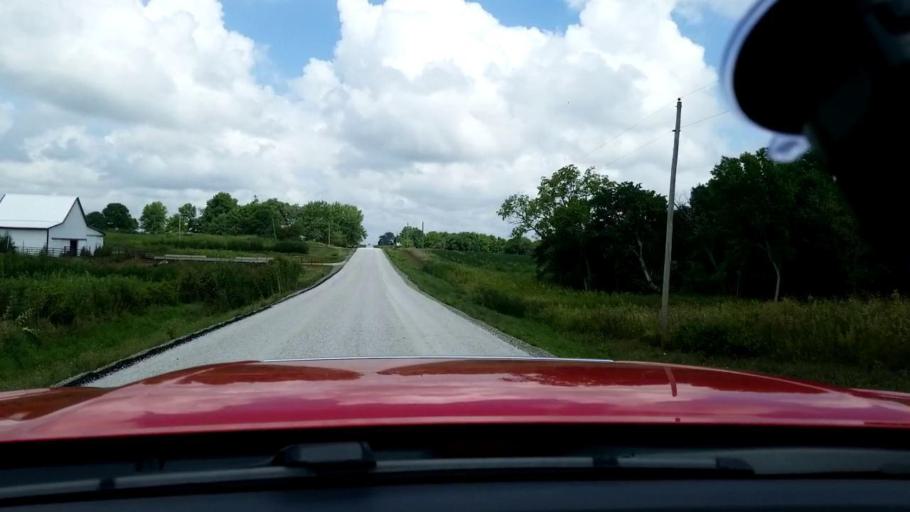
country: US
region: Iowa
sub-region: Decatur County
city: Lamoni
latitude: 40.6312
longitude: -94.0532
